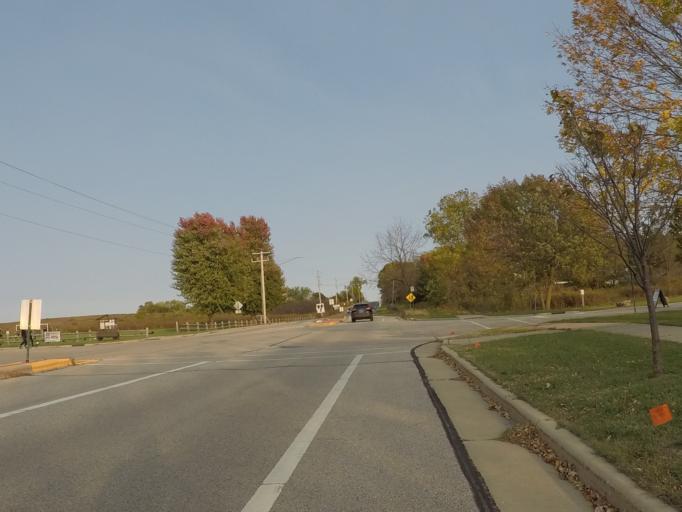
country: US
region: Wisconsin
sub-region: Dane County
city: Verona
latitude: 43.0014
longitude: -89.5250
